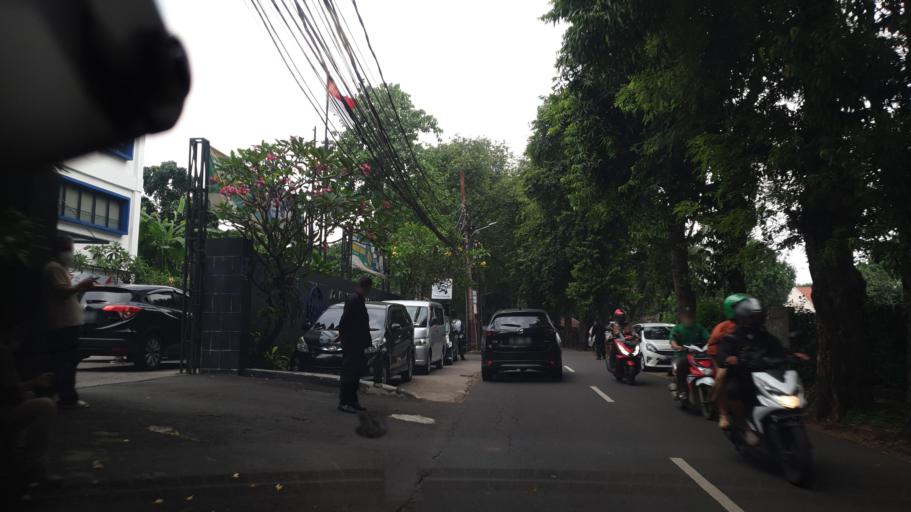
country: ID
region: West Java
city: Pamulang
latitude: -6.3049
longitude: 106.7779
